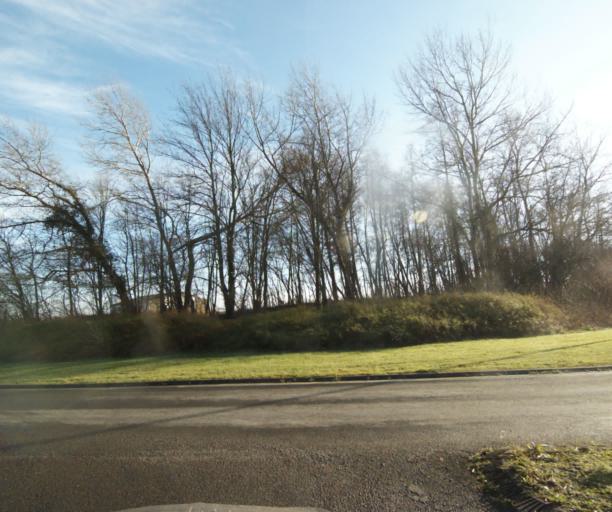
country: FR
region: Nord-Pas-de-Calais
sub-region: Departement du Nord
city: Famars
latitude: 50.3091
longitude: 3.5172
